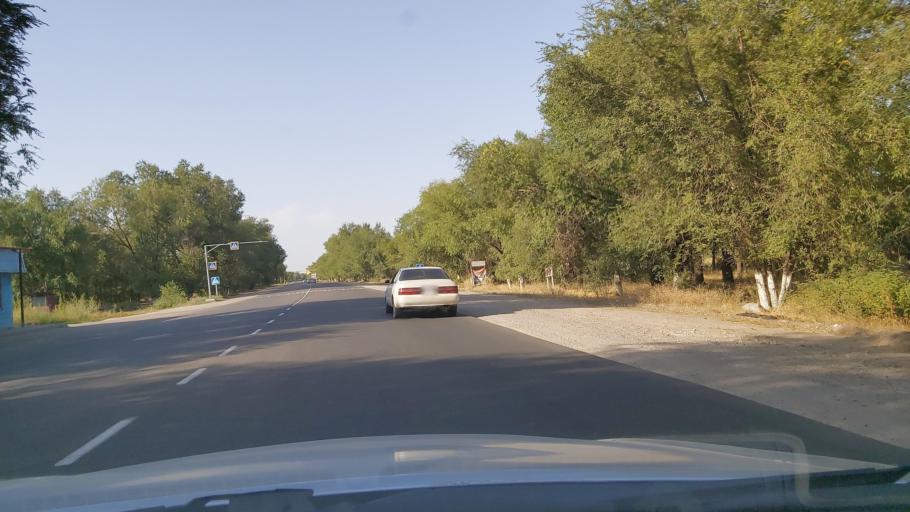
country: KZ
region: Almaty Oblysy
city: Energeticheskiy
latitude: 43.5510
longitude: 77.0527
